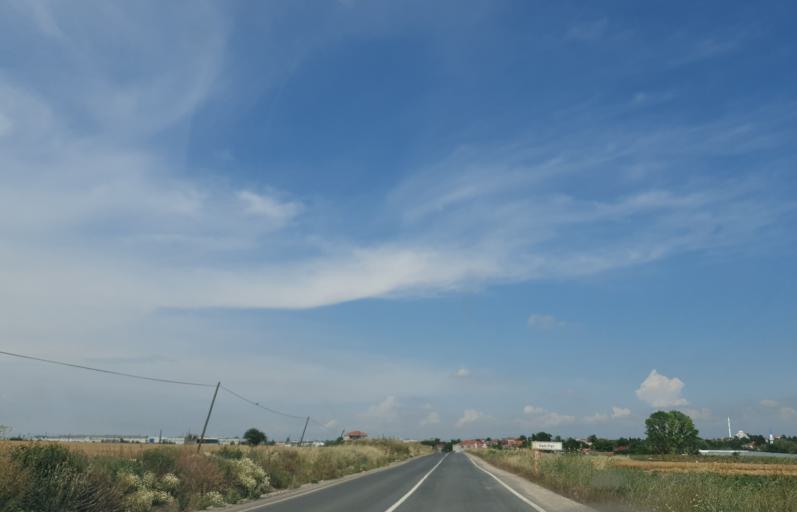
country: TR
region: Kirklareli
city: Buyukkaristiran
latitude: 41.2575
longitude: 27.6319
